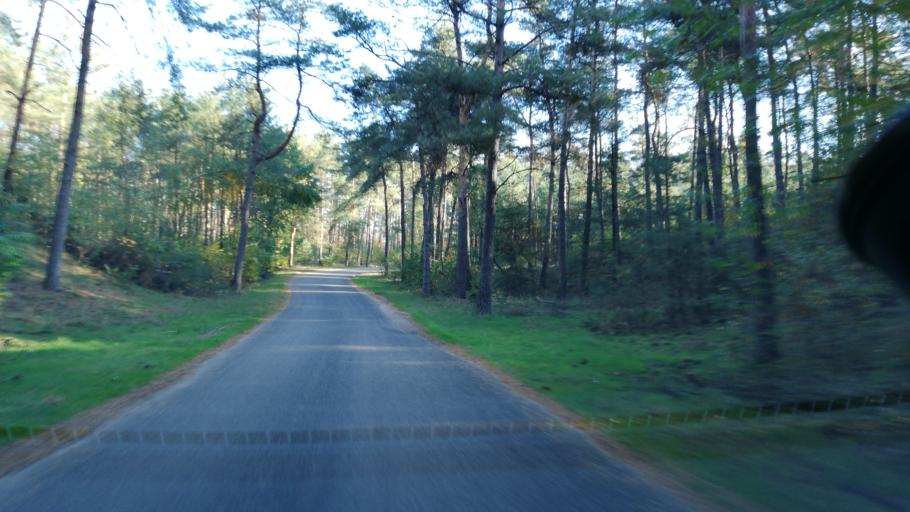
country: NL
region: Gelderland
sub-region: Gemeente Ede
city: Harskamp
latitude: 52.1721
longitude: 5.7531
